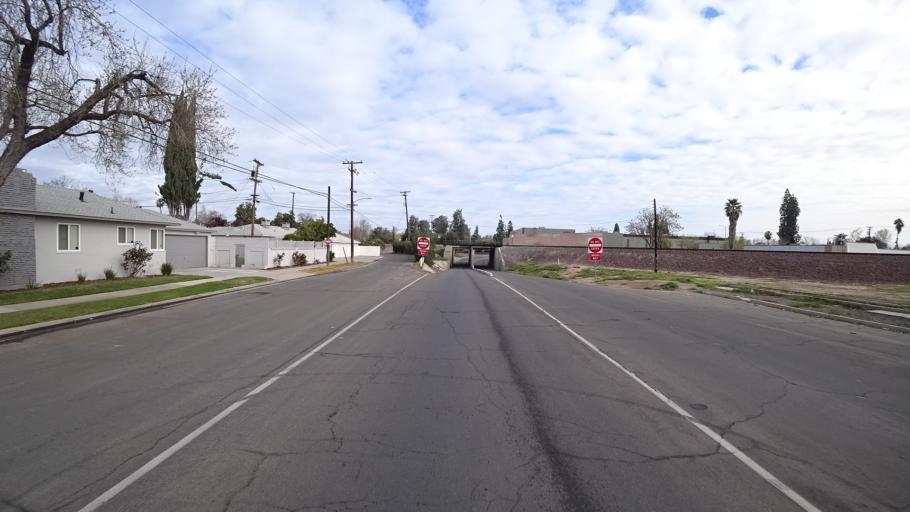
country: US
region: California
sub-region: Fresno County
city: Fresno
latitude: 36.7770
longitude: -119.8012
